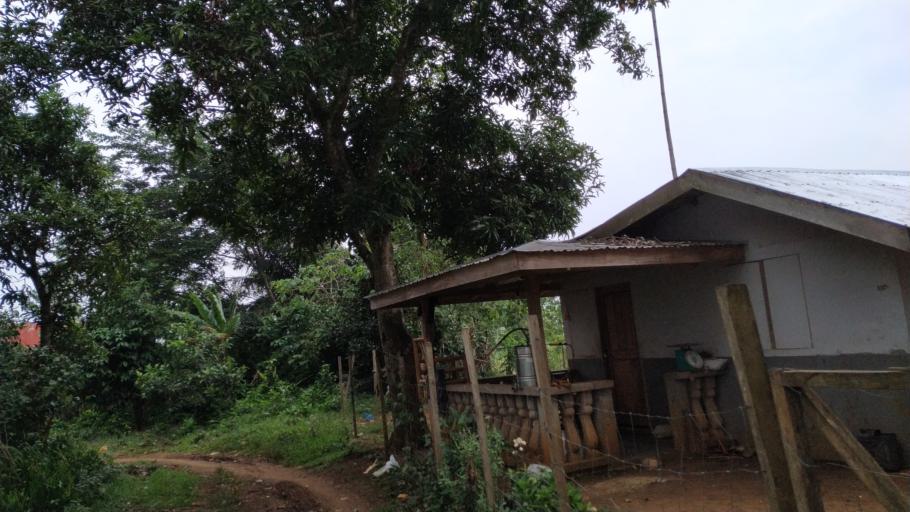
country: PH
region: Western Visayas
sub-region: Province of Negros Occidental
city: Quezon
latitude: 10.4208
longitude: 123.2415
